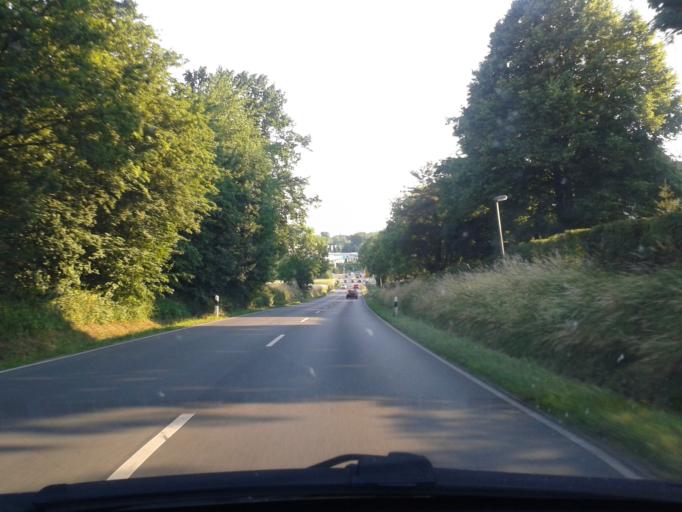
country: DE
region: North Rhine-Westphalia
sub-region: Regierungsbezirk Detmold
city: Detmold
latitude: 51.9505
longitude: 8.9031
